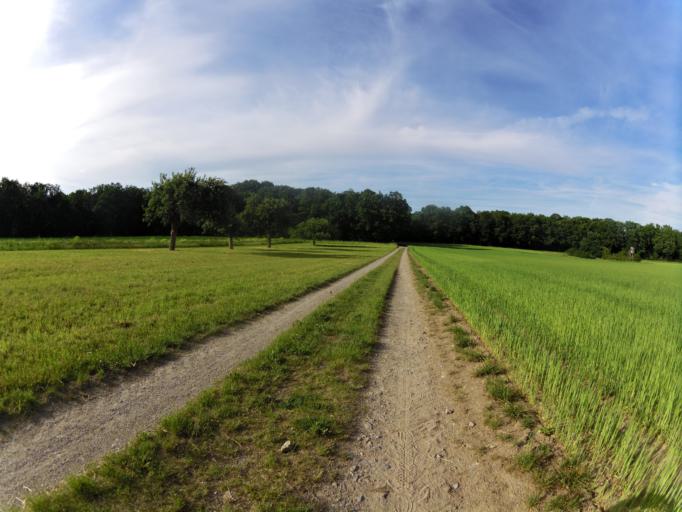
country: DE
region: Bavaria
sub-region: Regierungsbezirk Unterfranken
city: Frickenhausen
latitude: 49.6932
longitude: 10.0741
